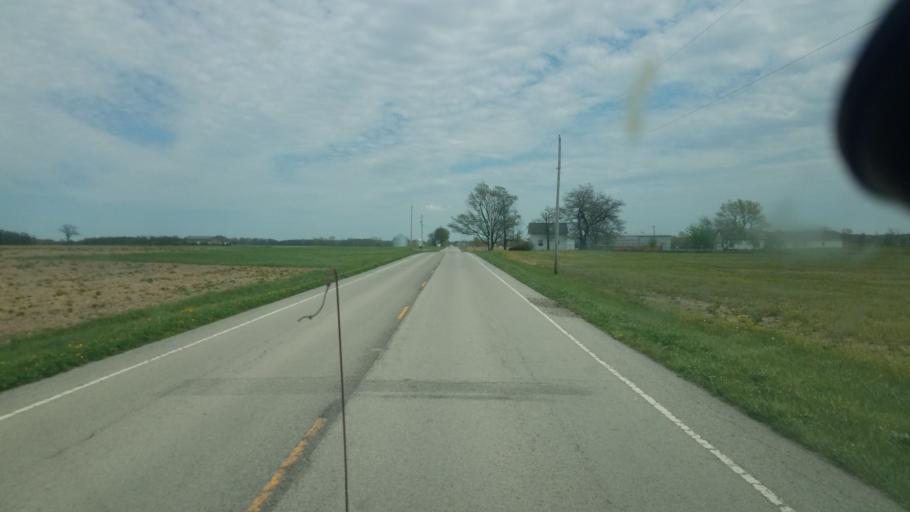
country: US
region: Ohio
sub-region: Hancock County
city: Arlington
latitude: 40.8339
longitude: -83.7231
